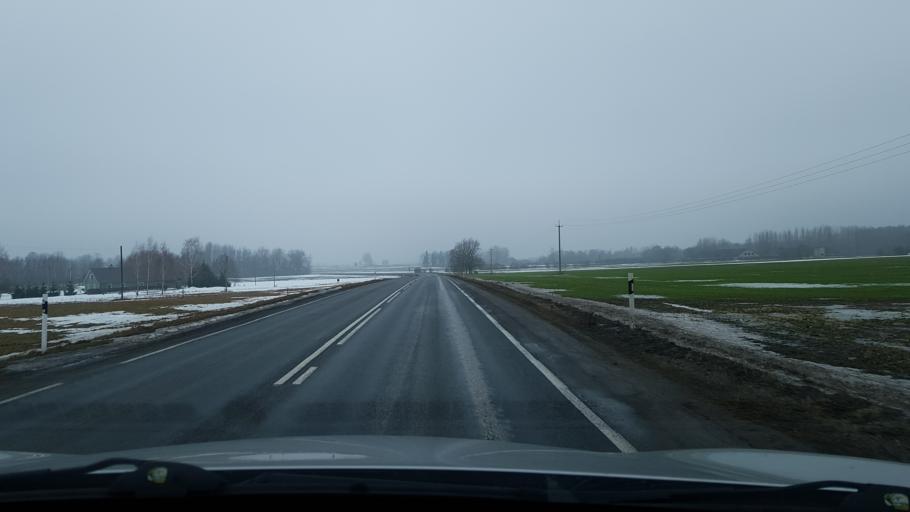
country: EE
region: Viljandimaa
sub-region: Viiratsi vald
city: Viiratsi
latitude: 58.2476
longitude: 25.8472
